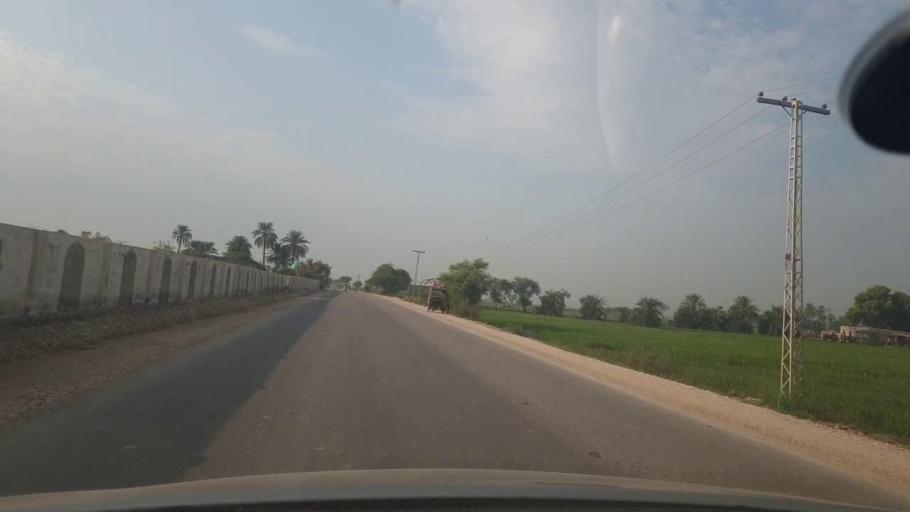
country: PK
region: Sindh
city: Jacobabad
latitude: 28.1943
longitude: 68.3676
